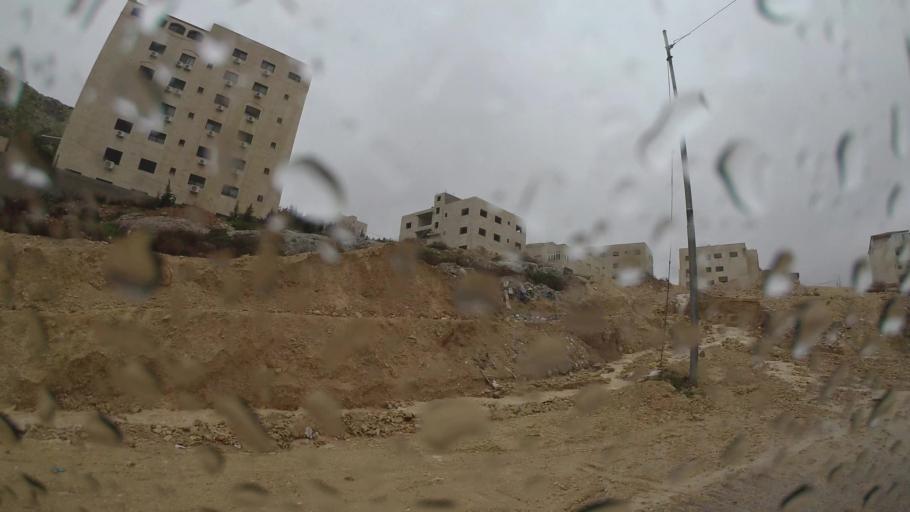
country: JO
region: Amman
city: Al Jubayhah
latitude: 32.0168
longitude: 35.8961
